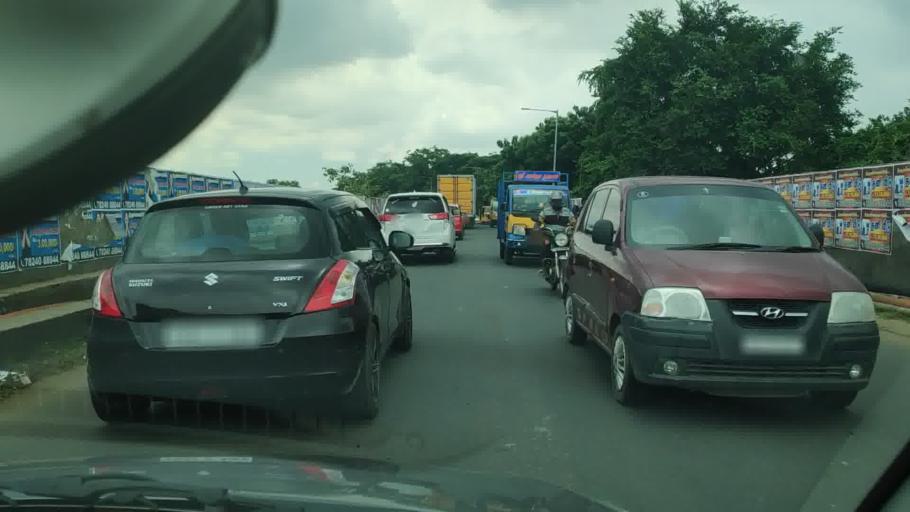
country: IN
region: Tamil Nadu
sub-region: Thiruvallur
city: Ambattur
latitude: 13.1144
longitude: 80.1482
